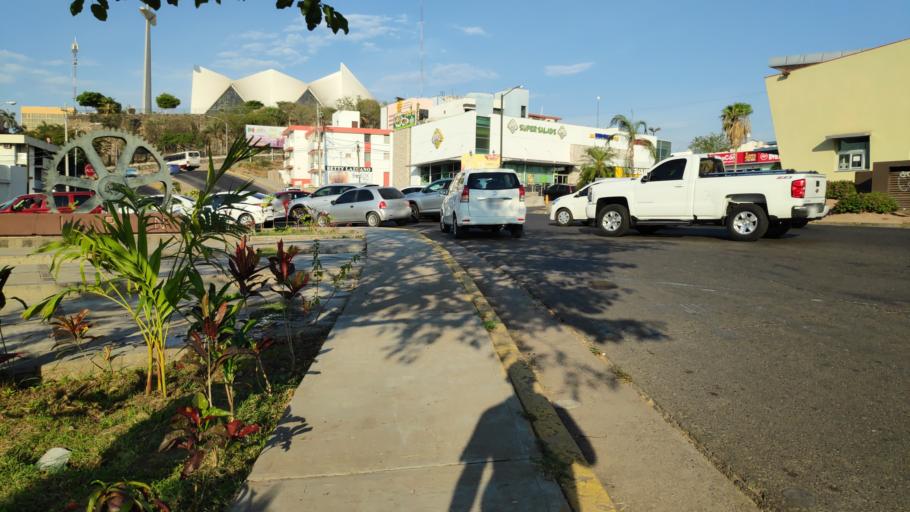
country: MX
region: Sinaloa
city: Culiacan
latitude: 24.7894
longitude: -107.3954
